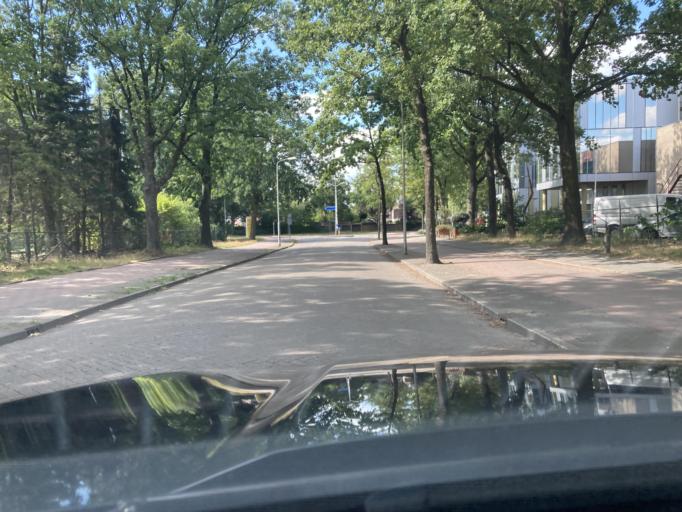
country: NL
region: North Brabant
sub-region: Gemeente Eindhoven
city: Eindhoven
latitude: 51.4773
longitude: 5.4548
